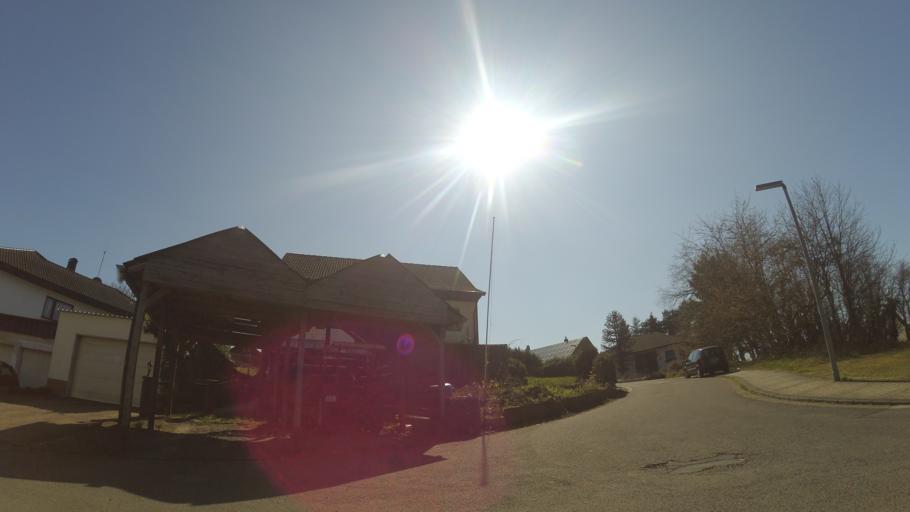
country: DE
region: Rheinland-Pfalz
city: Breitenbach
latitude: 49.4166
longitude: 7.2670
